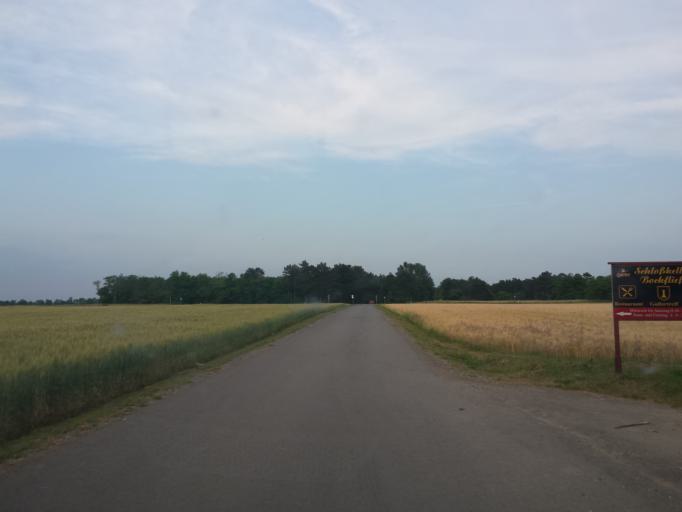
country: AT
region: Lower Austria
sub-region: Politischer Bezirk Mistelbach
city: Gross-Engersdorf
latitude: 48.3286
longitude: 16.5834
